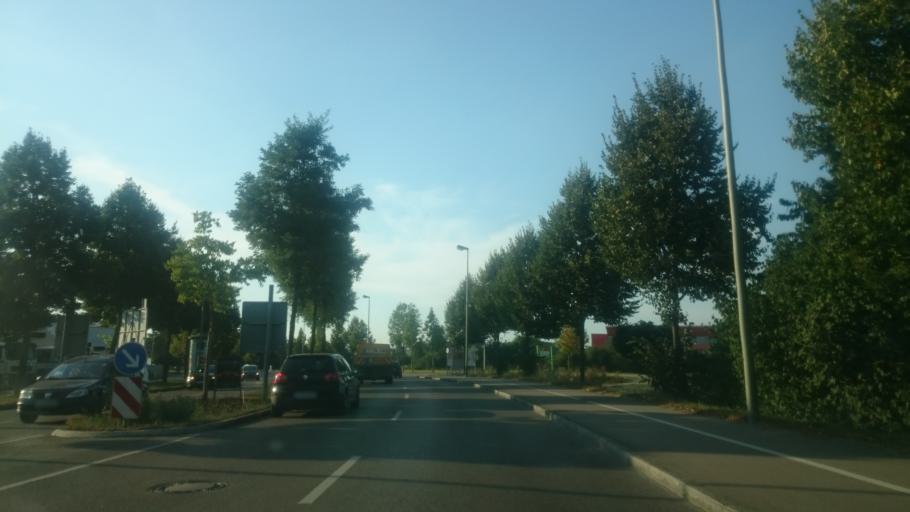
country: DE
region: Bavaria
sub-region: Swabia
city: Augsburg
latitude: 48.3966
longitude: 10.9305
